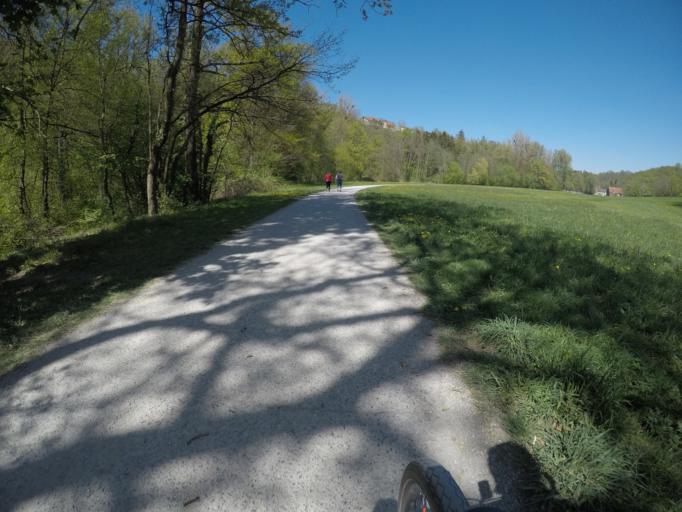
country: DE
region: Baden-Wuerttemberg
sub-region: Regierungsbezirk Stuttgart
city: Waiblingen
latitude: 48.8592
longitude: 9.3013
